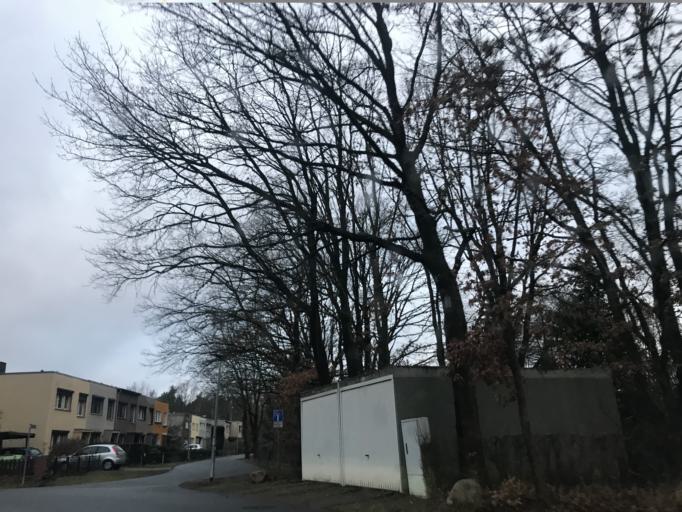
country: DE
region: Brandenburg
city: Rheinsberg
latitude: 53.0926
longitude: 12.8958
